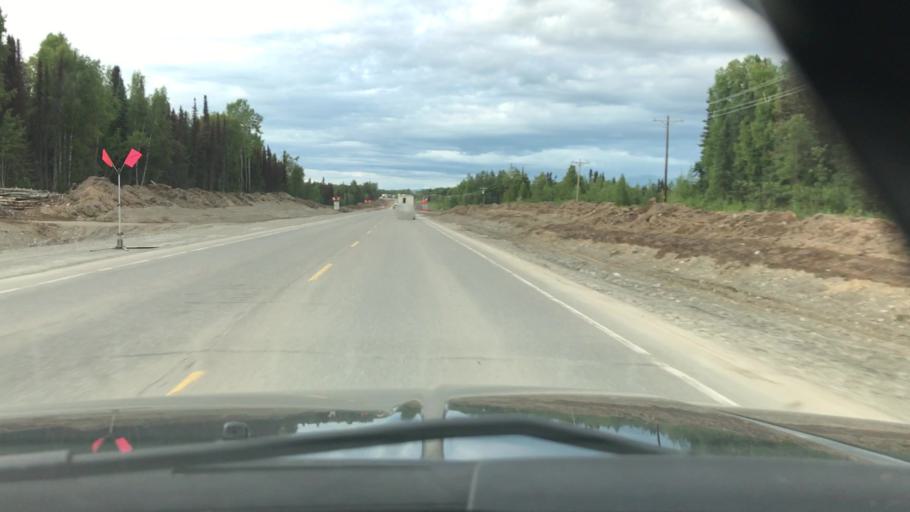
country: US
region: Alaska
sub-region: Matanuska-Susitna Borough
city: Y
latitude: 62.1188
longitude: -150.0480
